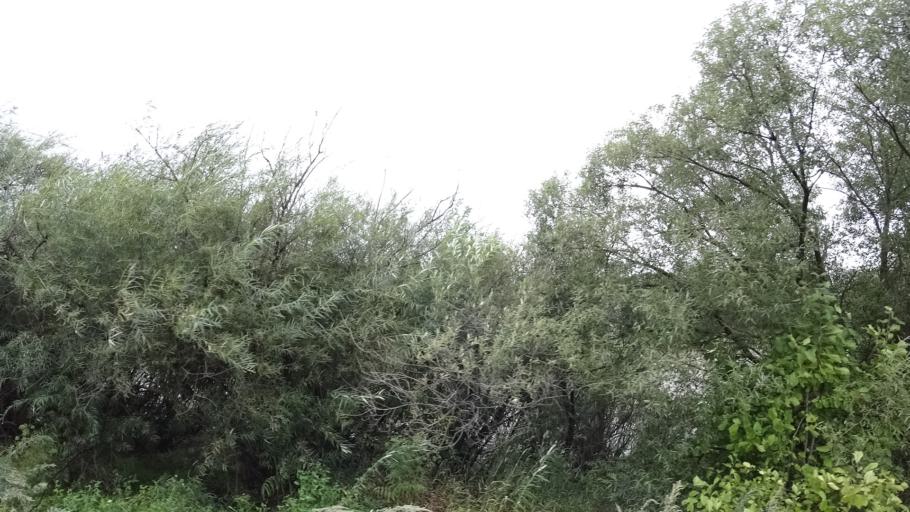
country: RU
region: Primorskiy
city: Monastyrishche
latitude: 44.2730
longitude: 132.4055
